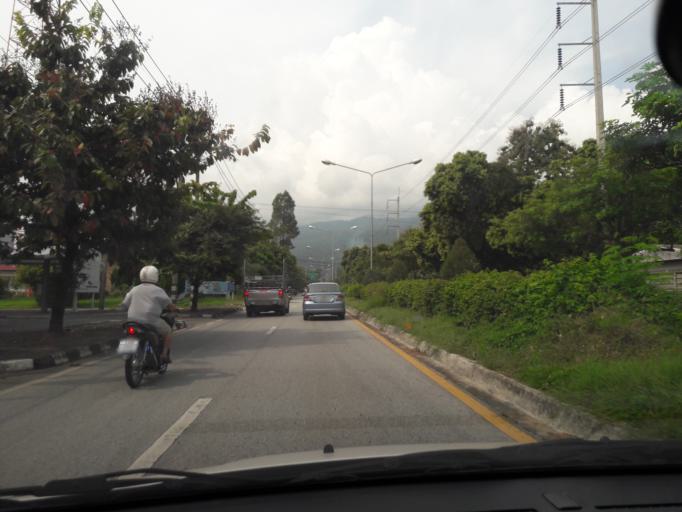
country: TH
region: Chiang Mai
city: Chiang Mai
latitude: 18.8414
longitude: 98.9697
